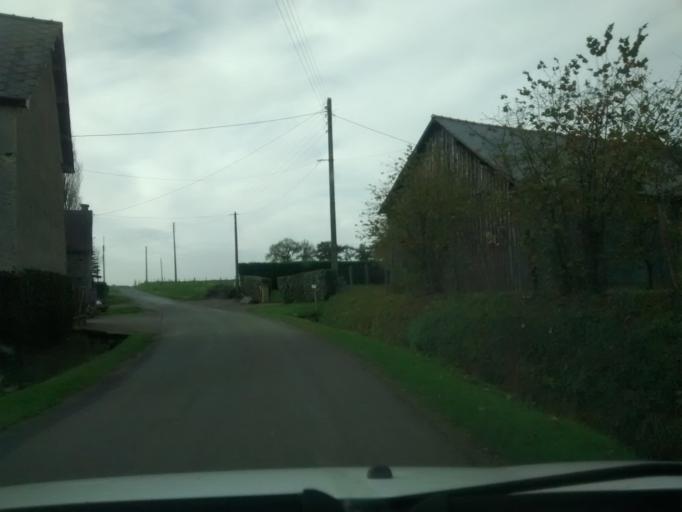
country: FR
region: Brittany
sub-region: Departement d'Ille-et-Vilaine
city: Brece
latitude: 48.1211
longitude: -1.4806
